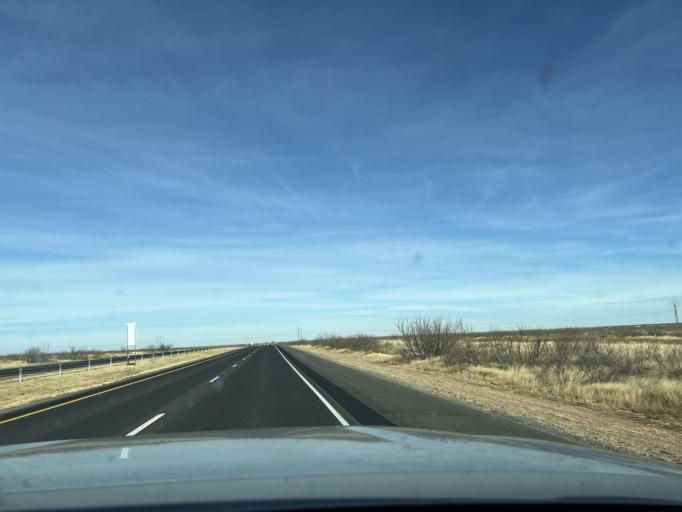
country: US
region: Texas
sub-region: Ector County
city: Gardendale
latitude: 32.0971
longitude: -102.4539
